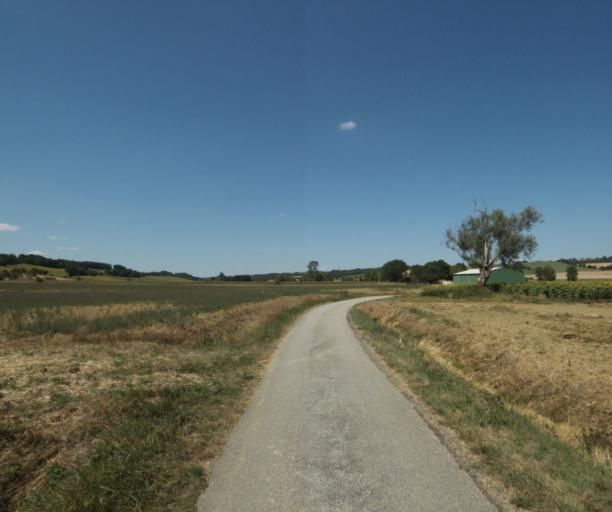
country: FR
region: Midi-Pyrenees
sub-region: Departement de la Haute-Garonne
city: Saint-Felix-Lauragais
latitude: 43.4826
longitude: 1.8761
